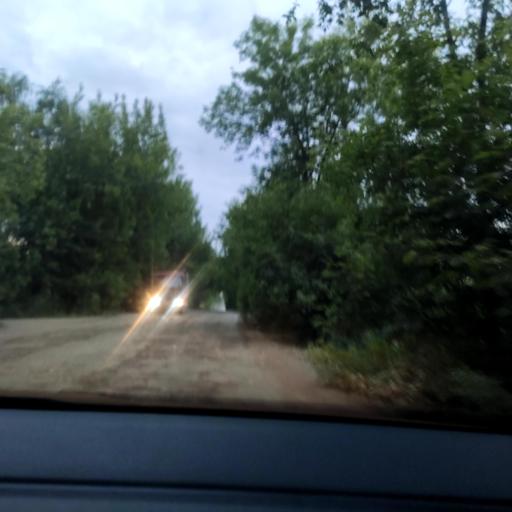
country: RU
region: Moskovskaya
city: Chornaya
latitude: 55.7229
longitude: 38.0495
